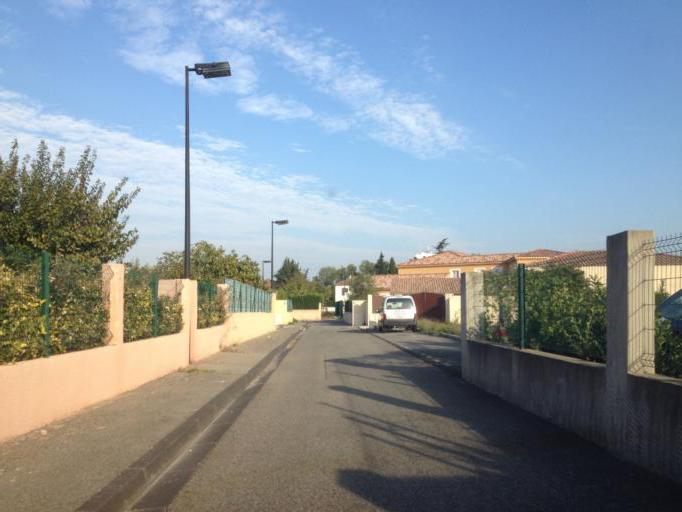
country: FR
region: Provence-Alpes-Cote d'Azur
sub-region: Departement du Vaucluse
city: Orange
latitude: 44.1496
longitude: 4.8014
